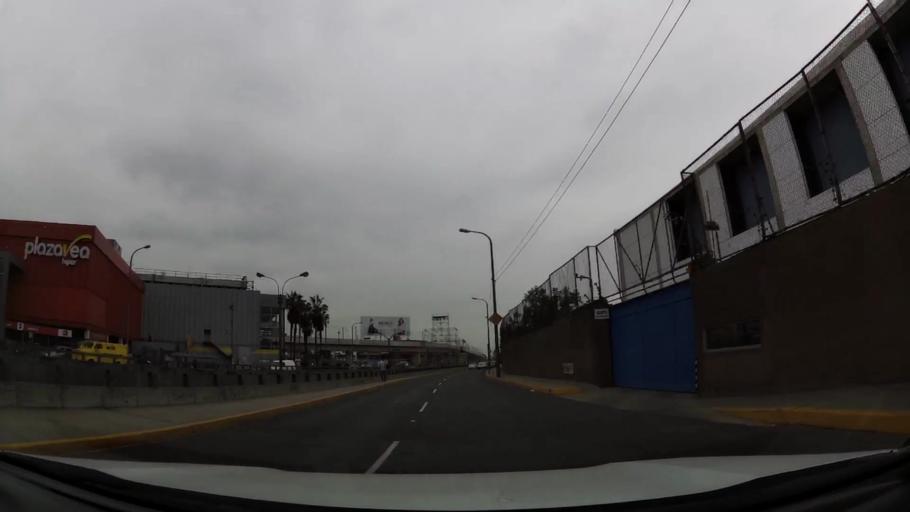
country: PE
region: Lima
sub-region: Lima
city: Surco
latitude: -12.1277
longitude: -77.0021
